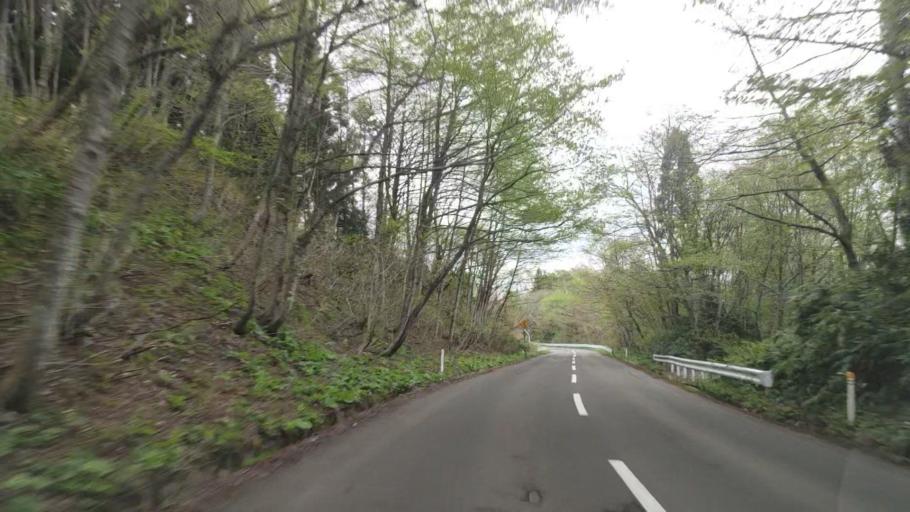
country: JP
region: Akita
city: Hanawa
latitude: 40.3782
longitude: 140.7911
